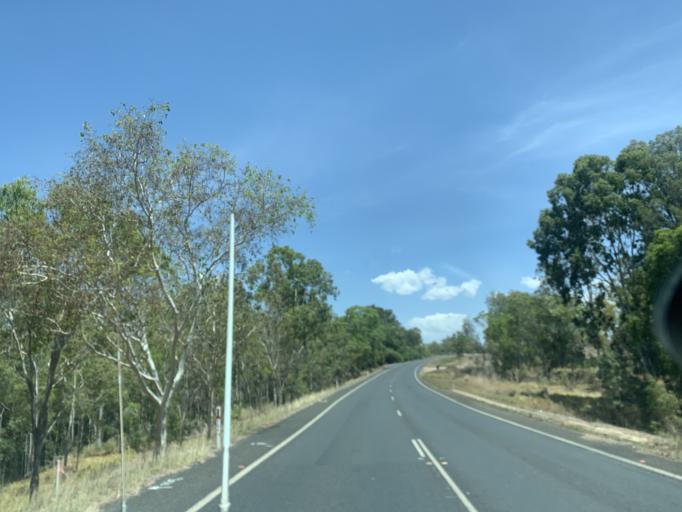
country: AU
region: Queensland
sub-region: Tablelands
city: Mareeba
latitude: -16.9577
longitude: 145.5397
